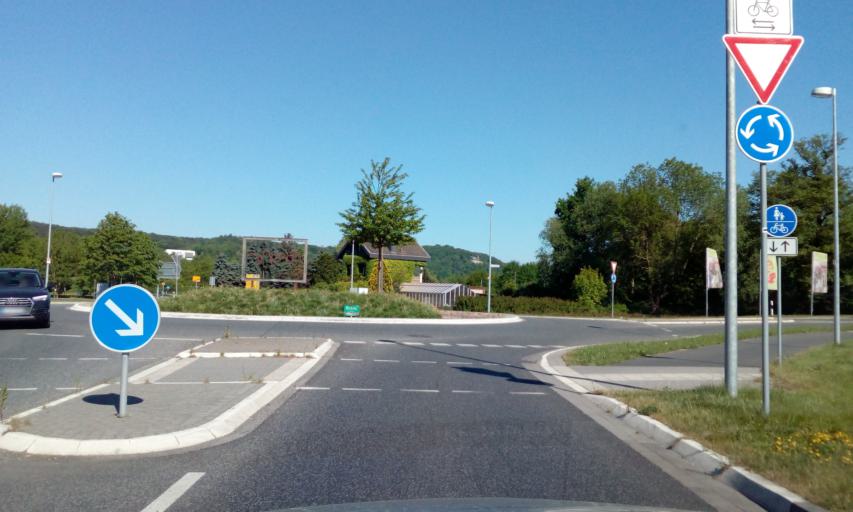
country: DE
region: Rheinland-Pfalz
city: Rheinbreitbach
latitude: 50.6261
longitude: 7.2228
